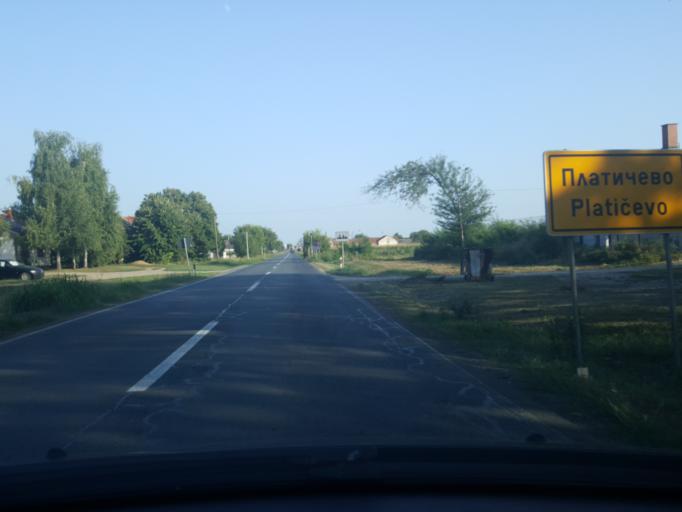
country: RS
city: Platicevo
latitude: 44.8349
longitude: 19.7732
